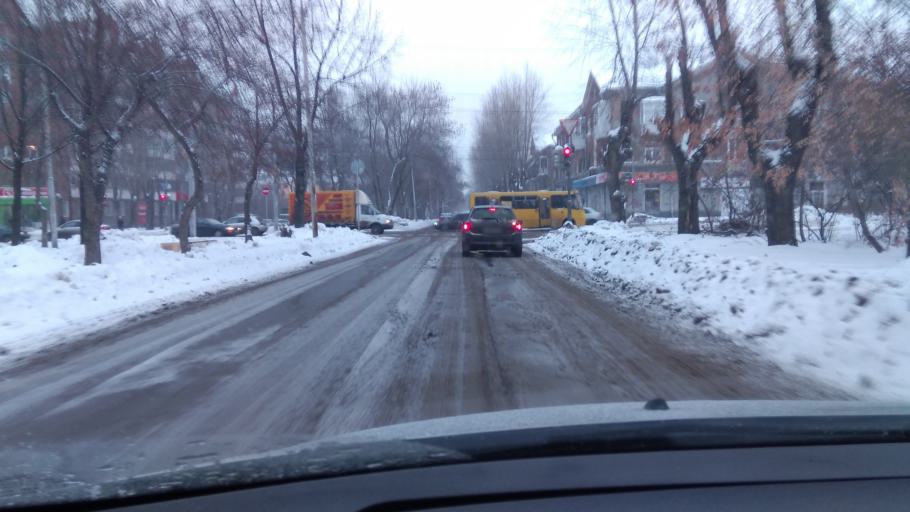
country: RU
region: Sverdlovsk
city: Yekaterinburg
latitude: 56.8948
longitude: 60.5859
